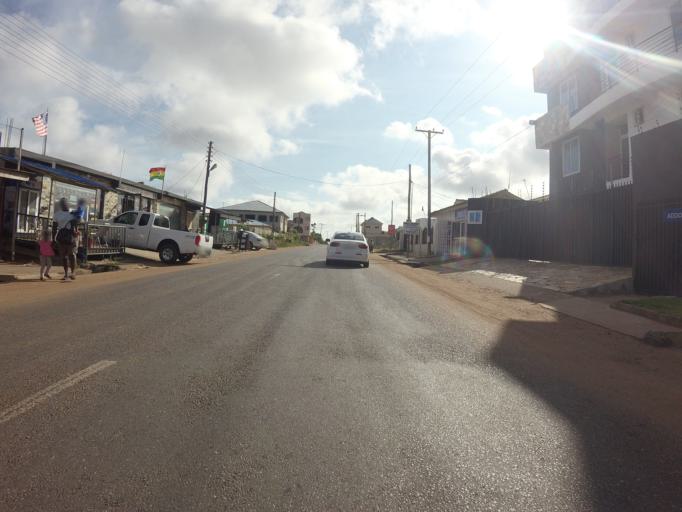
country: GH
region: Greater Accra
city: Teshi Old Town
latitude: 5.5853
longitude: -0.1422
